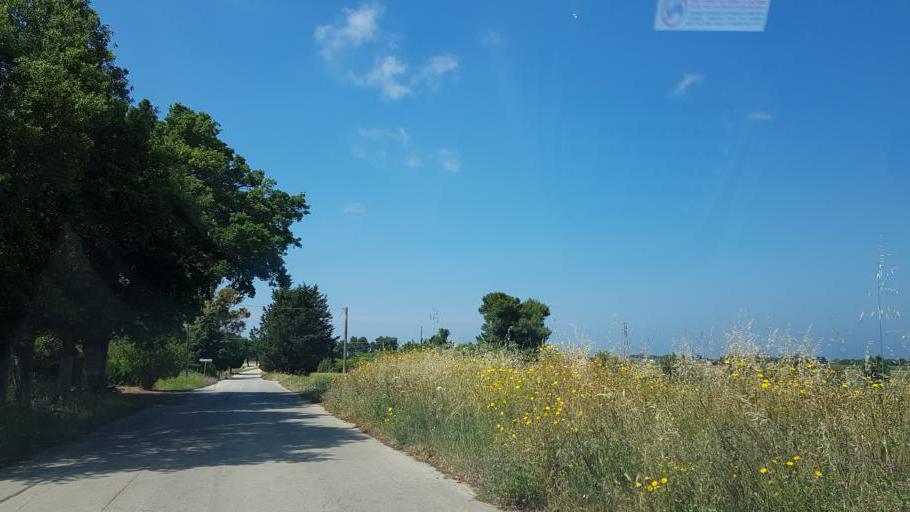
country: IT
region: Apulia
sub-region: Provincia di Brindisi
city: Brindisi
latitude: 40.6516
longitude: 17.8543
